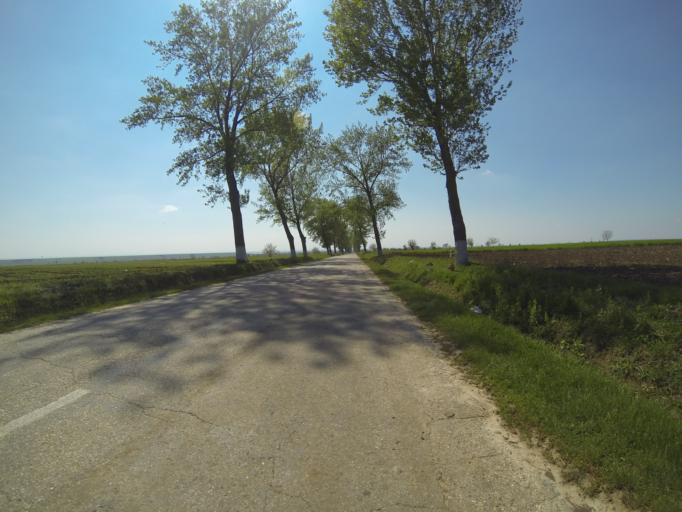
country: RO
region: Dolj
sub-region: Comuna Caraula
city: Caraula
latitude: 44.2000
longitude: 23.2764
